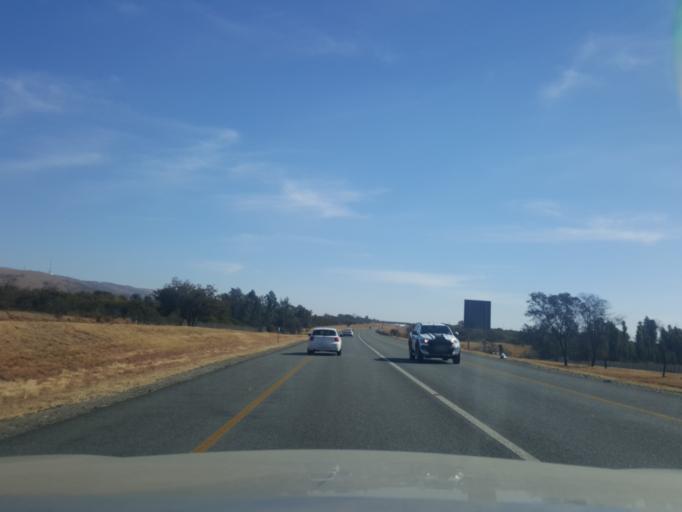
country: ZA
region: North-West
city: Ga-Rankuwa
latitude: -25.6573
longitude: 28.0289
